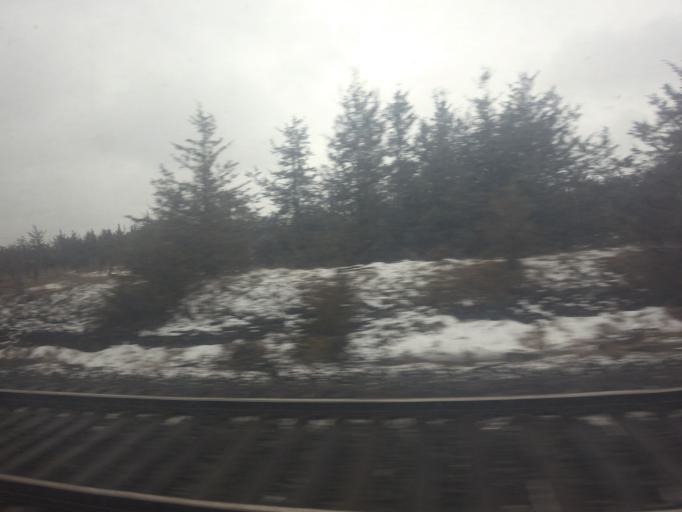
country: CA
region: Ontario
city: Belleville
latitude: 44.2052
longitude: -77.2299
